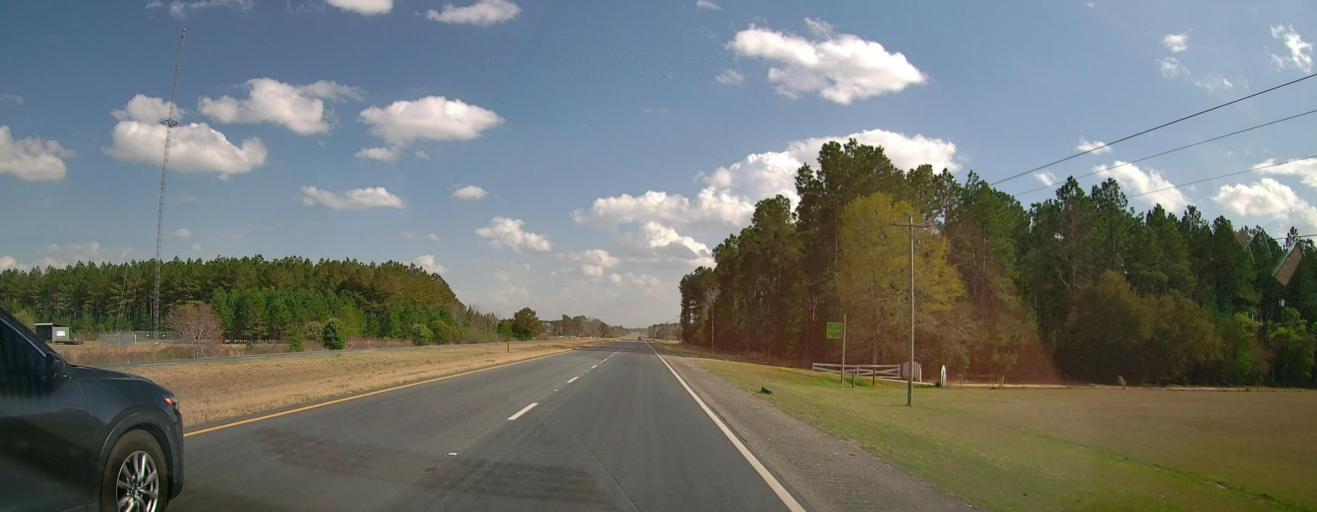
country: US
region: Georgia
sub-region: Dodge County
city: Eastman
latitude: 32.1473
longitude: -83.1375
